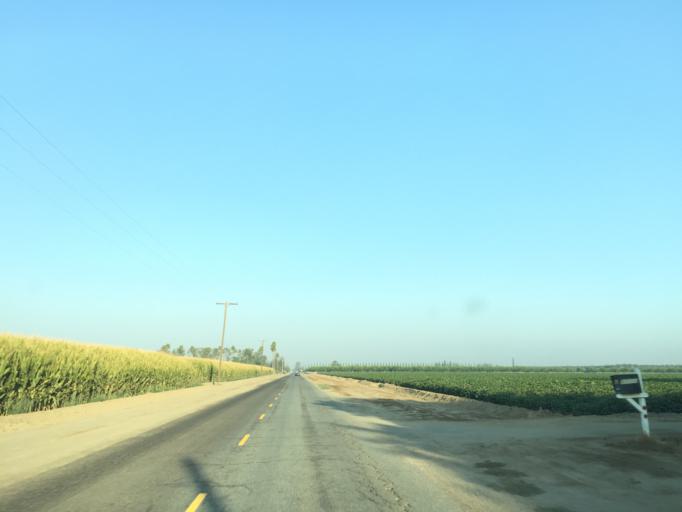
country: US
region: California
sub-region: Tulare County
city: Visalia
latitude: 36.3710
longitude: -119.2705
